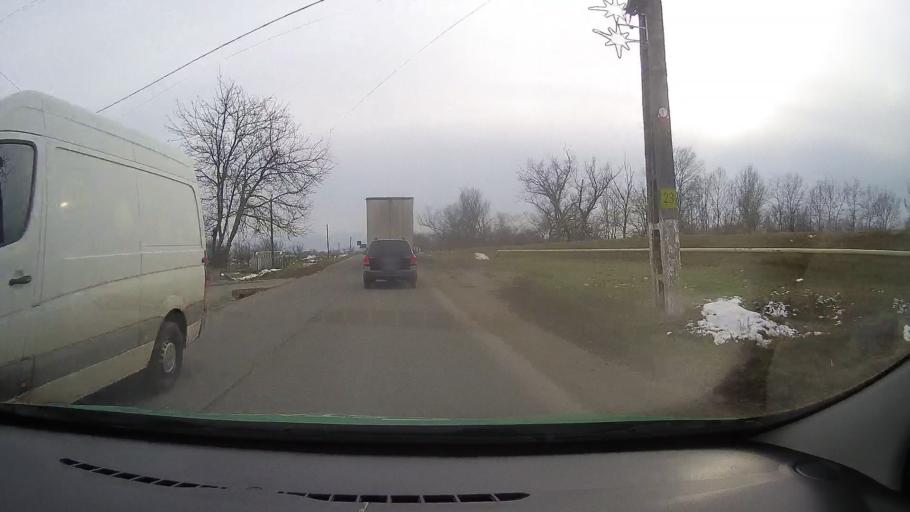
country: RO
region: Hunedoara
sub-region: Comuna Geoagiu
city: Geoagiu
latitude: 45.8997
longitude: 23.2248
